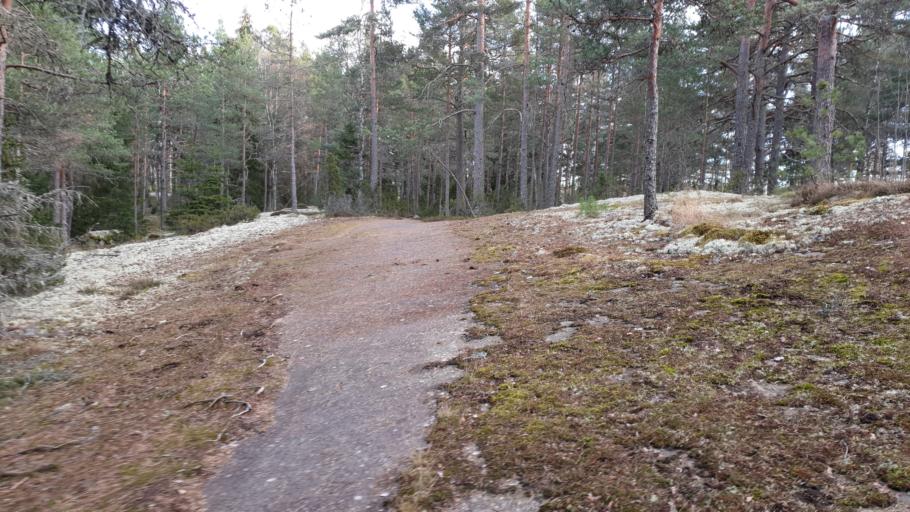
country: SE
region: Uppsala
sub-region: Enkopings Kommun
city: Grillby
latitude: 59.5989
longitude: 17.1618
